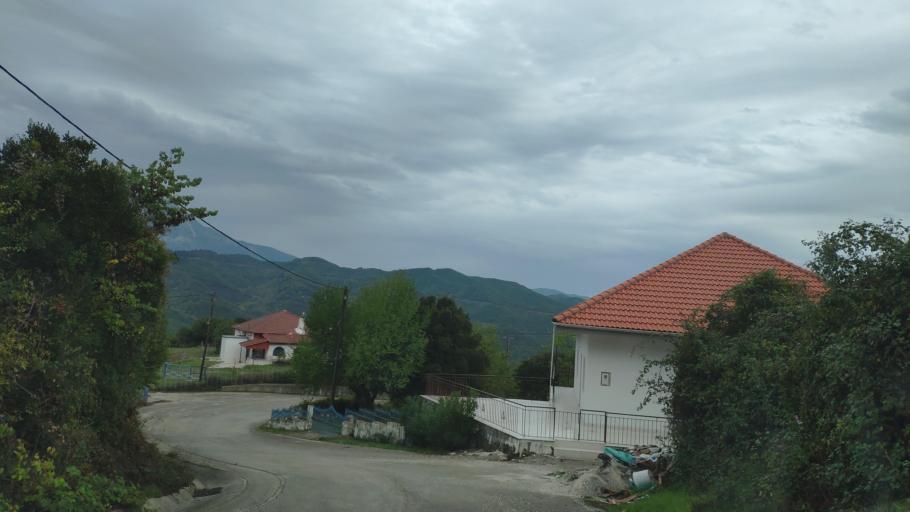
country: GR
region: Epirus
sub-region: Nomos Thesprotias
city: Paramythia
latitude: 39.4576
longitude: 20.6757
